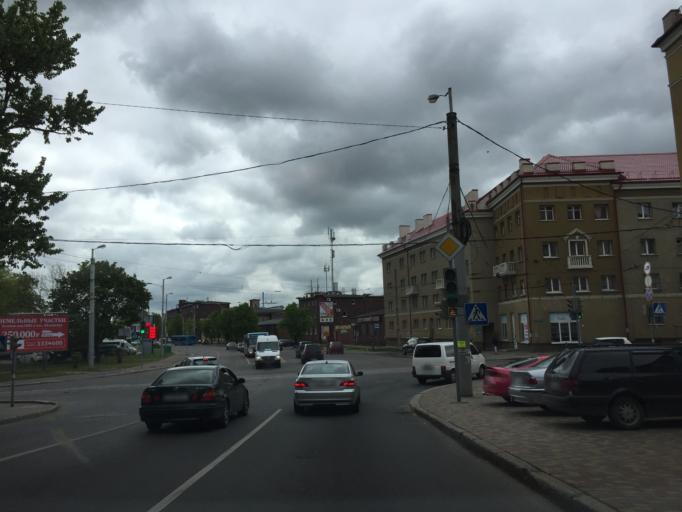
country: RU
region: Kaliningrad
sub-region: Gorod Kaliningrad
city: Kaliningrad
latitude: 54.6972
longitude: 20.4935
